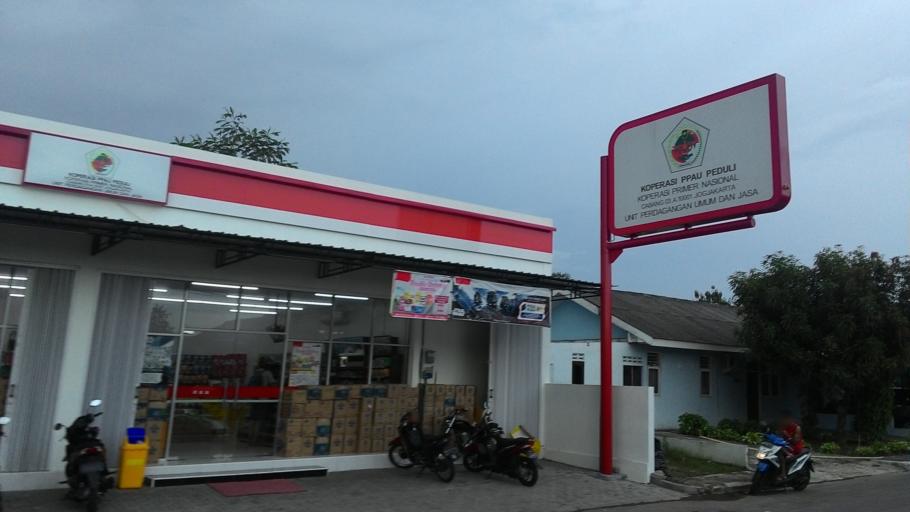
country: ID
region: Daerah Istimewa Yogyakarta
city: Depok
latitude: -7.7986
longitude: 110.4123
